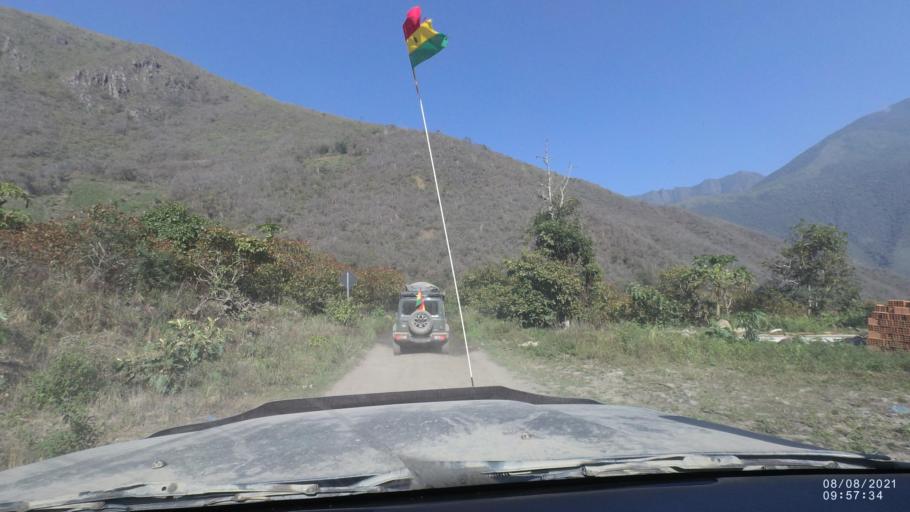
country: BO
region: La Paz
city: Quime
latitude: -16.6419
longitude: -66.7253
